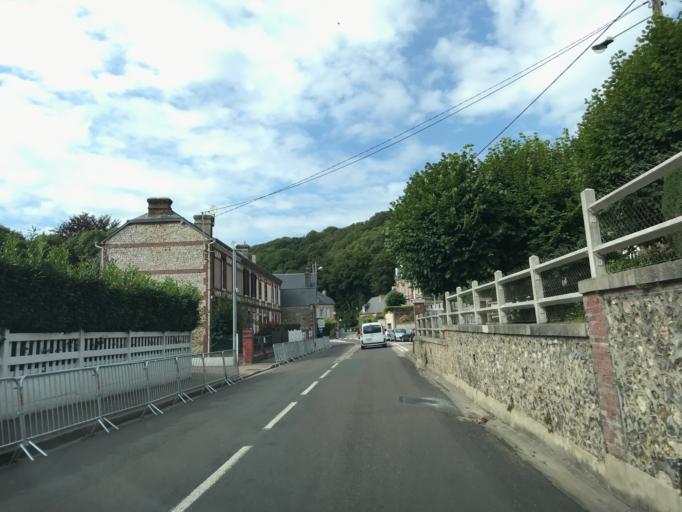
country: FR
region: Haute-Normandie
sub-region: Departement de la Seine-Maritime
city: Yport
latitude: 49.7355
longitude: 0.3178
